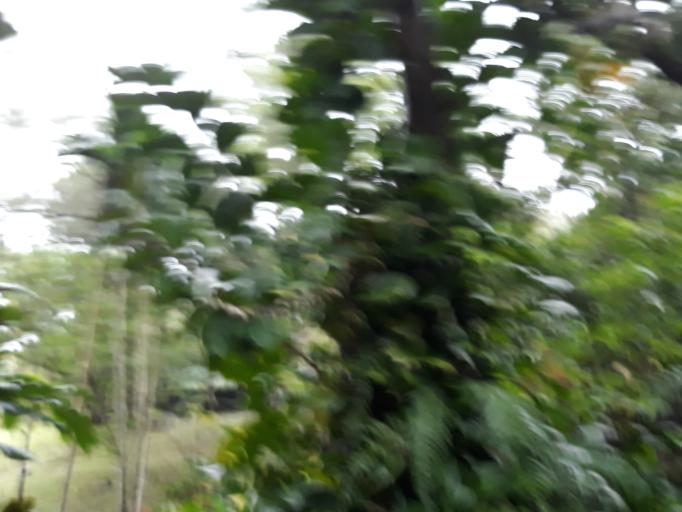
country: TW
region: Taipei
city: Taipei
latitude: 24.9953
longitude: 121.5847
